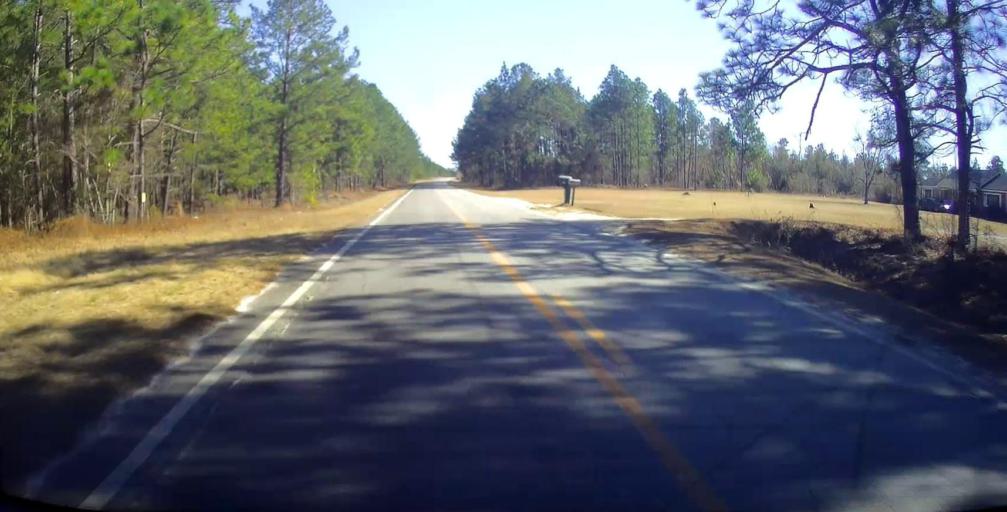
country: US
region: Georgia
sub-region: Crawford County
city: Roberta
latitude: 32.6357
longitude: -83.9970
